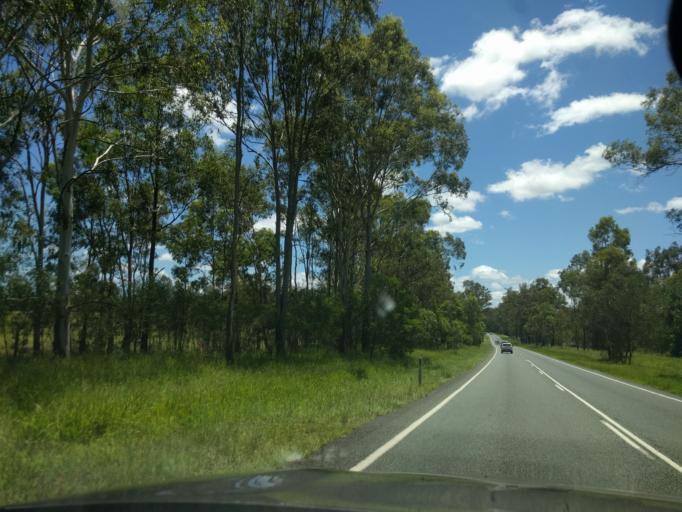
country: AU
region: Queensland
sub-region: Logan
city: Cedar Vale
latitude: -27.8514
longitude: 153.0147
